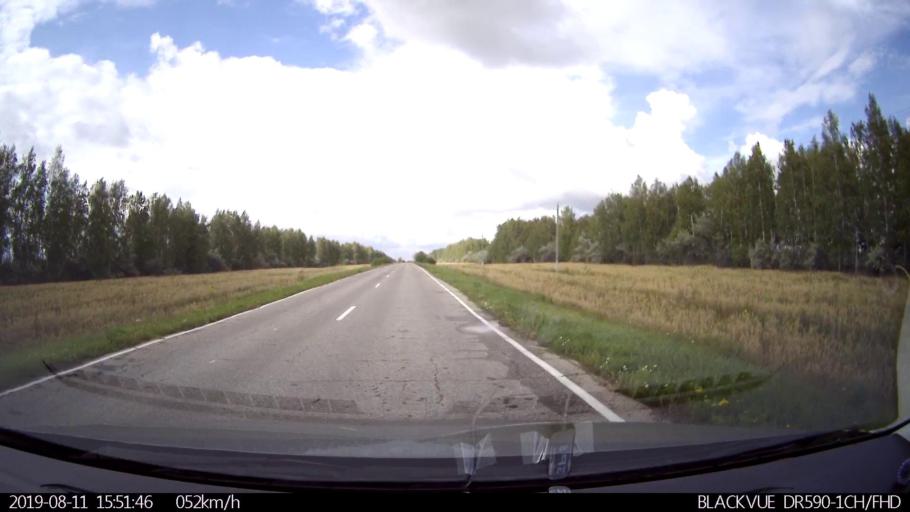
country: RU
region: Ulyanovsk
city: Ignatovka
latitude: 53.9214
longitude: 47.6562
